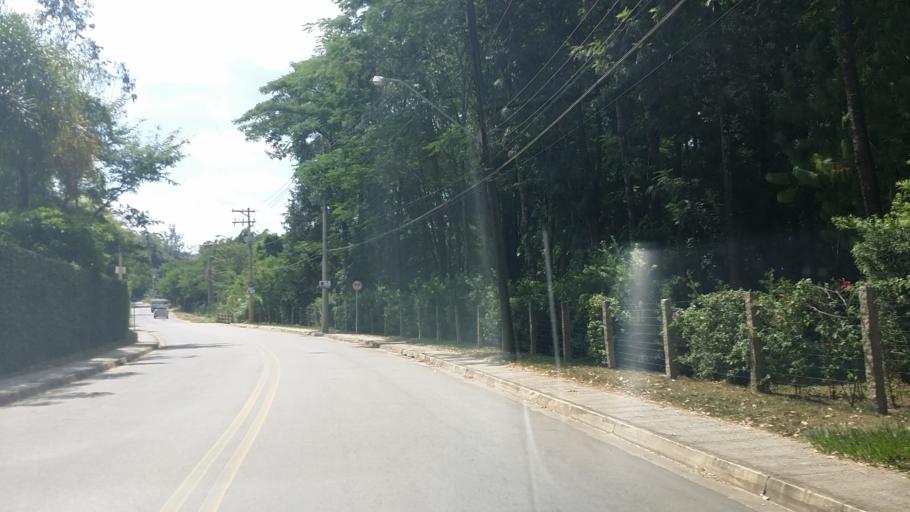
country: BR
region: Sao Paulo
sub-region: Itupeva
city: Itupeva
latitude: -23.1955
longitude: -47.0225
